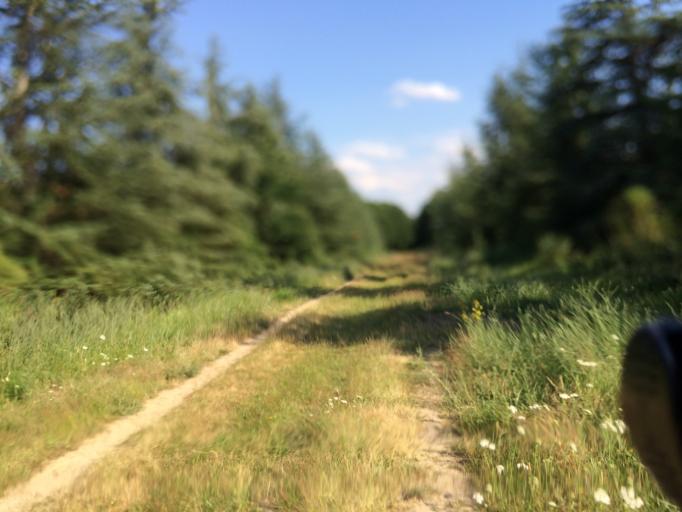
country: FR
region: Ile-de-France
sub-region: Departement de l'Essonne
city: Soisy-sur-Seine
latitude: 48.6749
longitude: 2.4524
